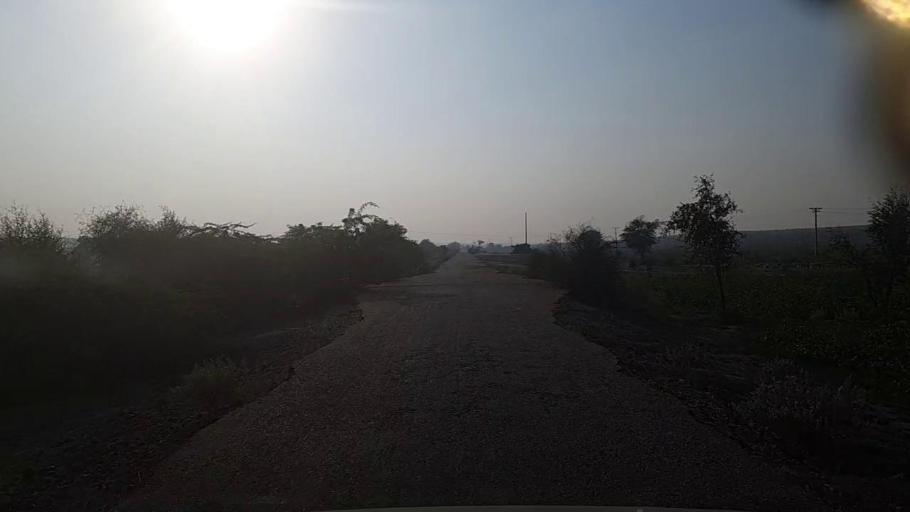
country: PK
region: Sindh
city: Pad Idan
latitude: 26.7166
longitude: 68.4875
